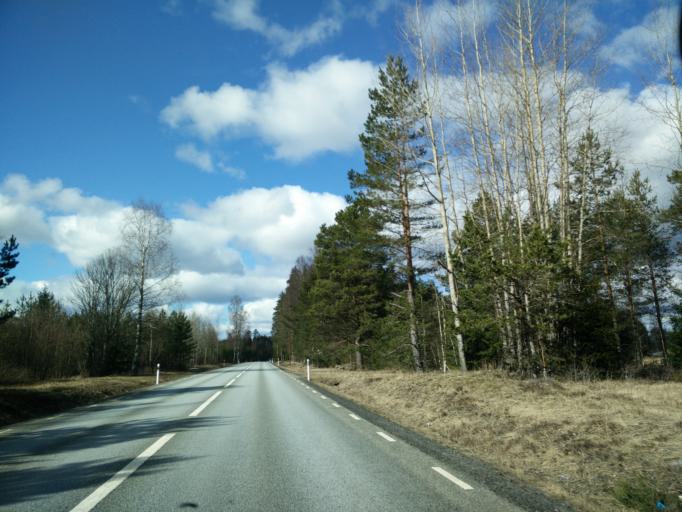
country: SE
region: Vaermland
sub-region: Munkfors Kommun
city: Munkfors
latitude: 59.9575
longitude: 13.5687
